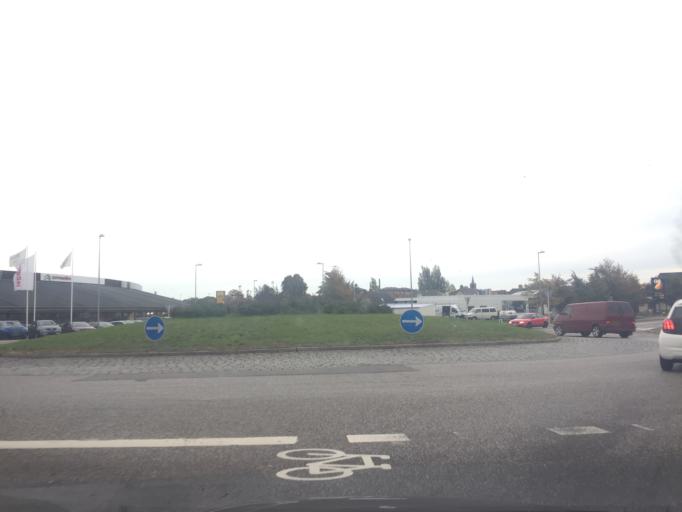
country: DK
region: Zealand
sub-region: Slagelse Kommune
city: Slagelse
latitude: 55.4111
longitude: 11.3375
